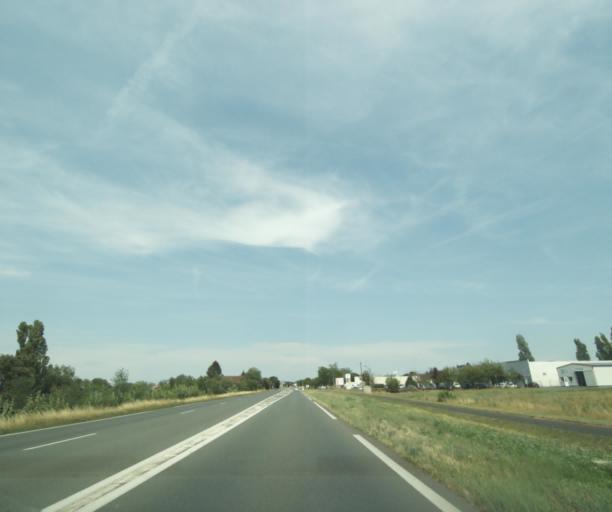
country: FR
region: Poitou-Charentes
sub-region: Departement de la Vienne
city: Dange-Saint-Romain
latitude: 46.9239
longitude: 0.5989
